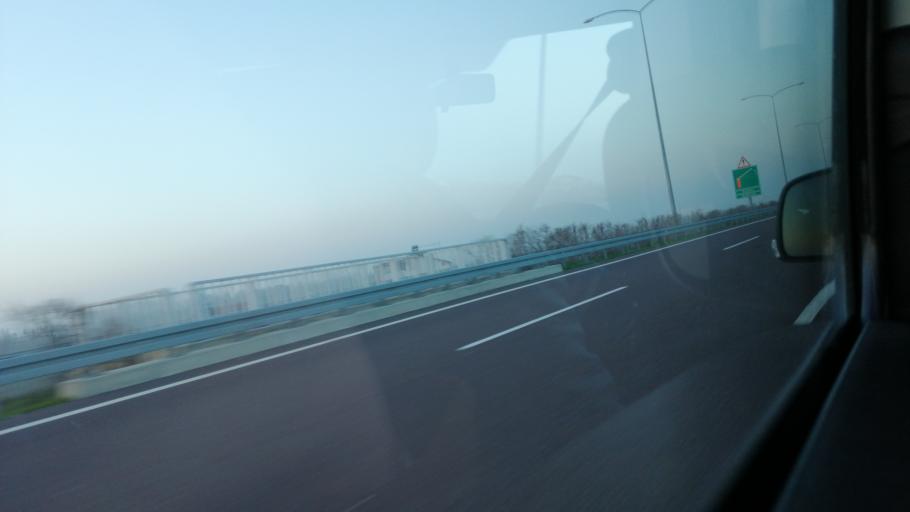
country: TR
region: Yalova
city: Altinova
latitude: 40.7089
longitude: 29.4953
